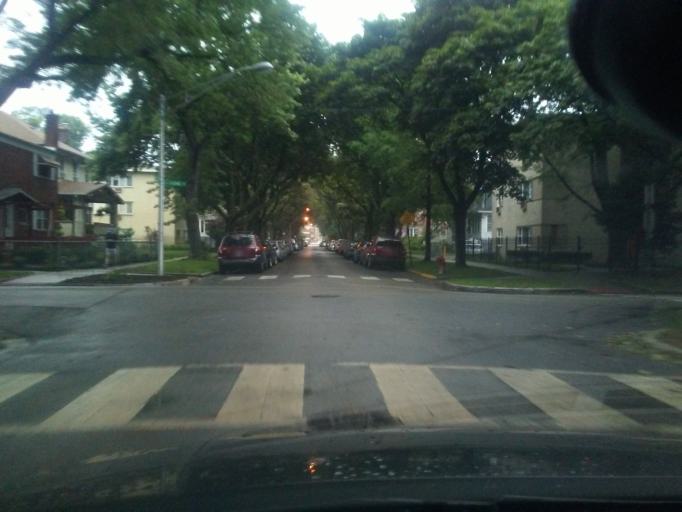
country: US
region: Illinois
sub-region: Cook County
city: Evanston
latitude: 41.9955
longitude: -87.6719
